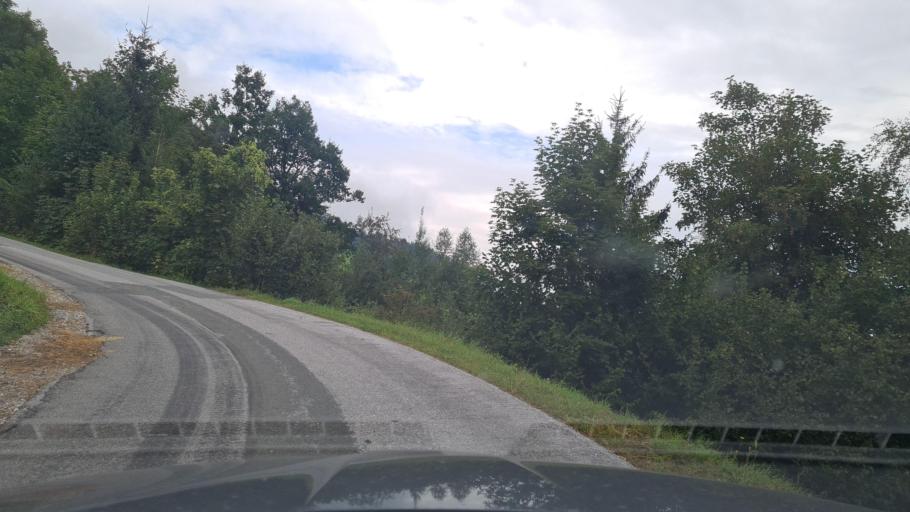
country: AT
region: Salzburg
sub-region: Politischer Bezirk Sankt Johann im Pongau
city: Sankt Johann im Pongau
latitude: 47.3578
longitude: 13.1910
